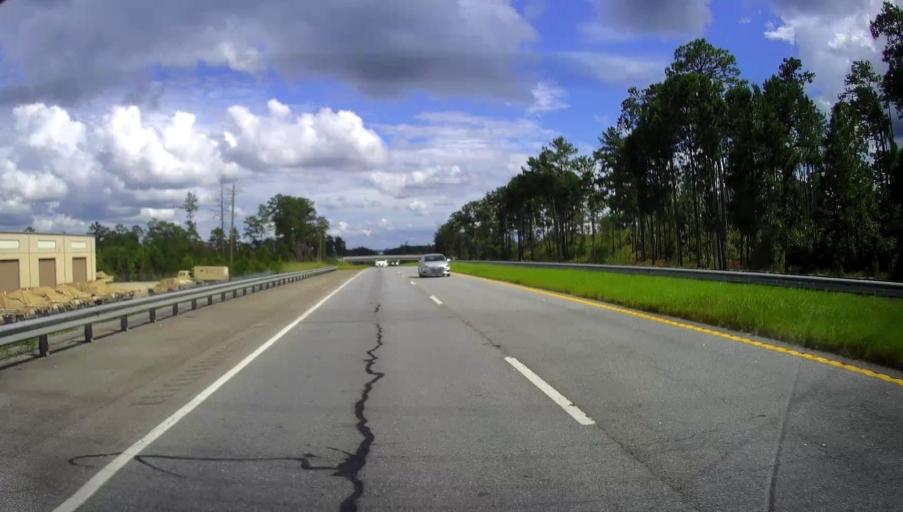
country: US
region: Georgia
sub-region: Chattahoochee County
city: Cusseta
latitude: 32.3650
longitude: -84.8494
